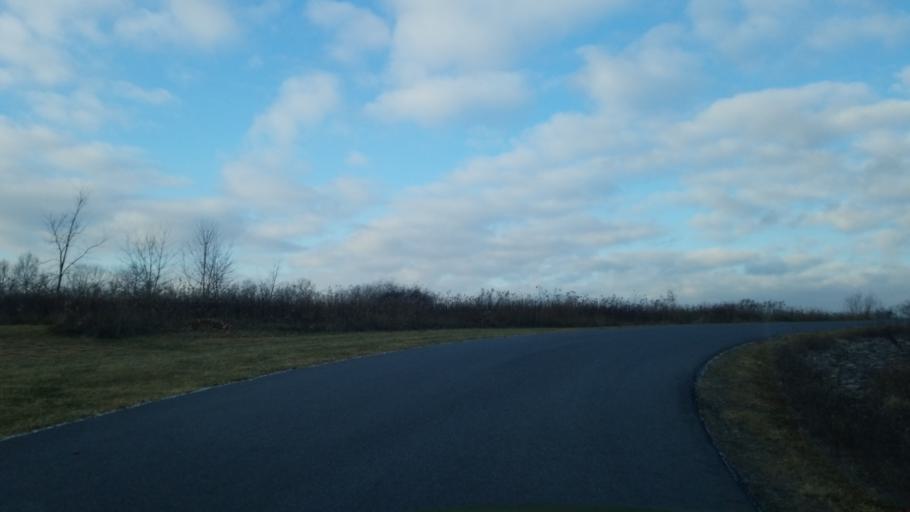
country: US
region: Pennsylvania
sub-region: Clearfield County
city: Clearfield
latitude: 41.0078
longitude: -78.4216
